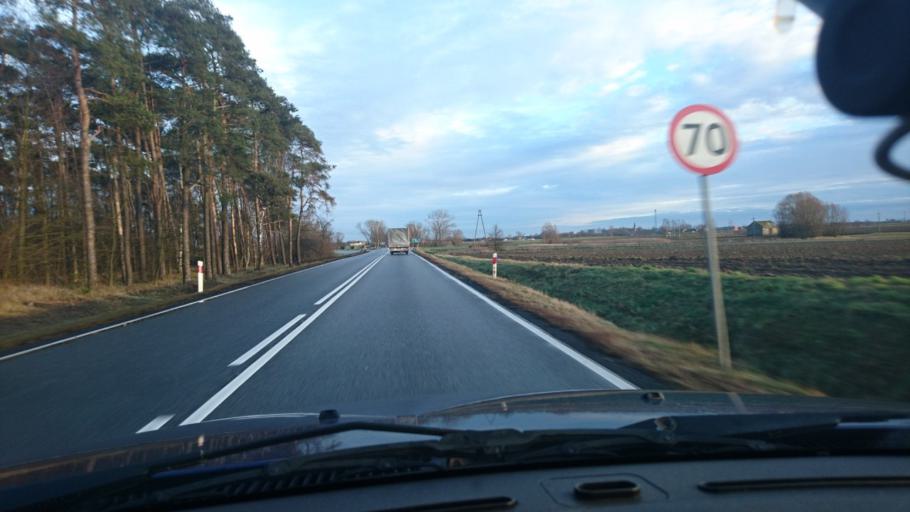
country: PL
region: Greater Poland Voivodeship
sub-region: Powiat kepinski
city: Leka Opatowska
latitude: 51.2220
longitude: 18.1257
